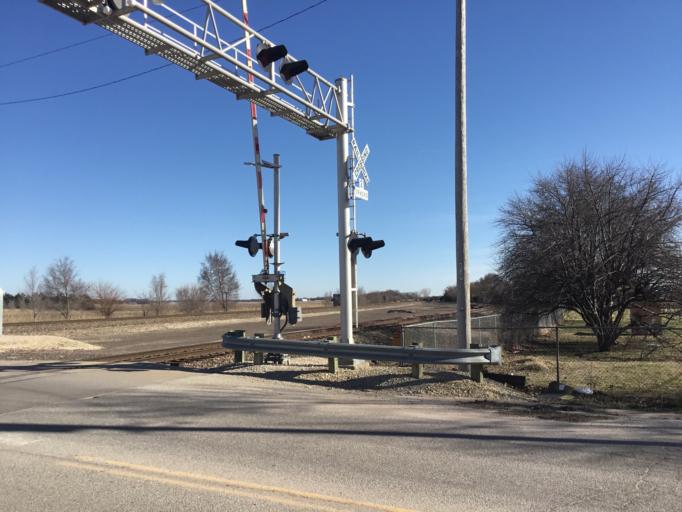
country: US
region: Kansas
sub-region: Harvey County
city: Sedgwick
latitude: 37.9123
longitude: -97.4226
